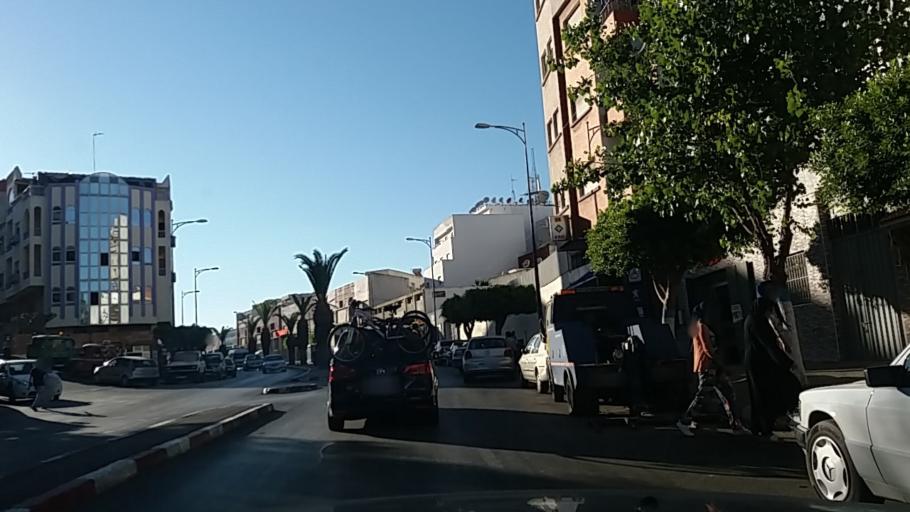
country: MA
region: Tanger-Tetouan
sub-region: Tanger-Assilah
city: Tangier
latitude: 35.7684
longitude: -5.8159
